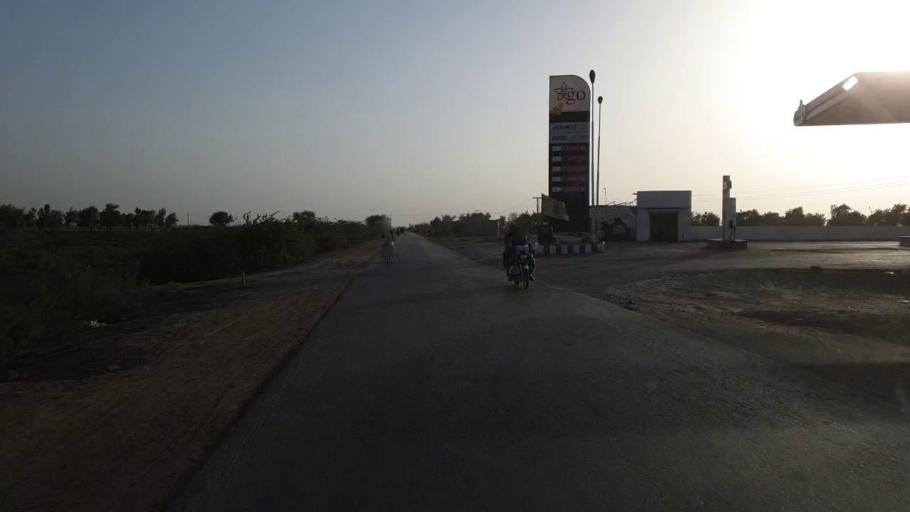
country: PK
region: Sindh
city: Jam Sahib
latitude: 26.2915
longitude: 68.6142
